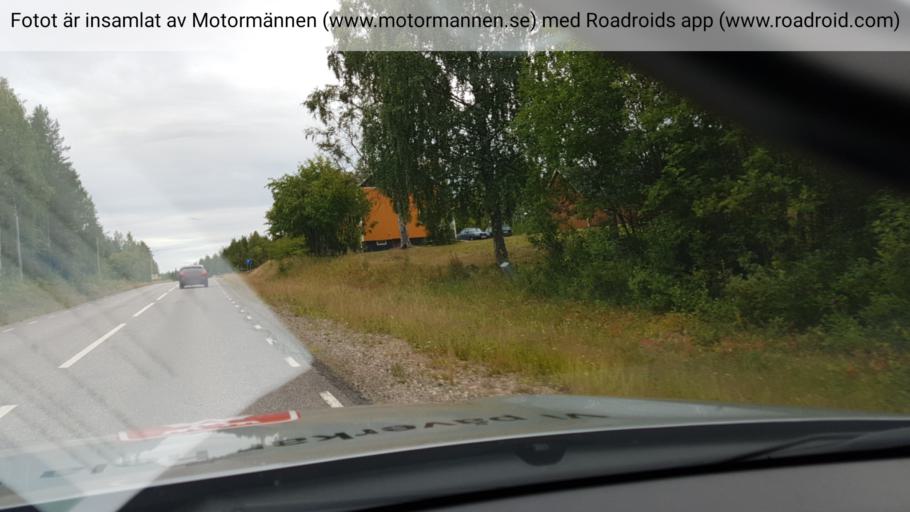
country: SE
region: Norrbotten
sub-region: Overkalix Kommun
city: OEverkalix
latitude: 66.5324
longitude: 22.7571
